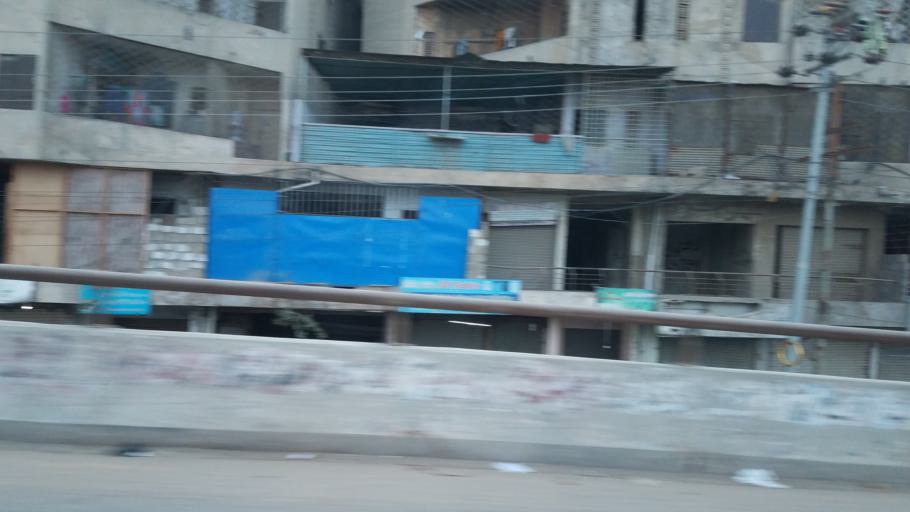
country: PK
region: Sindh
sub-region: Karachi District
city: Karachi
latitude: 24.9418
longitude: 67.0849
